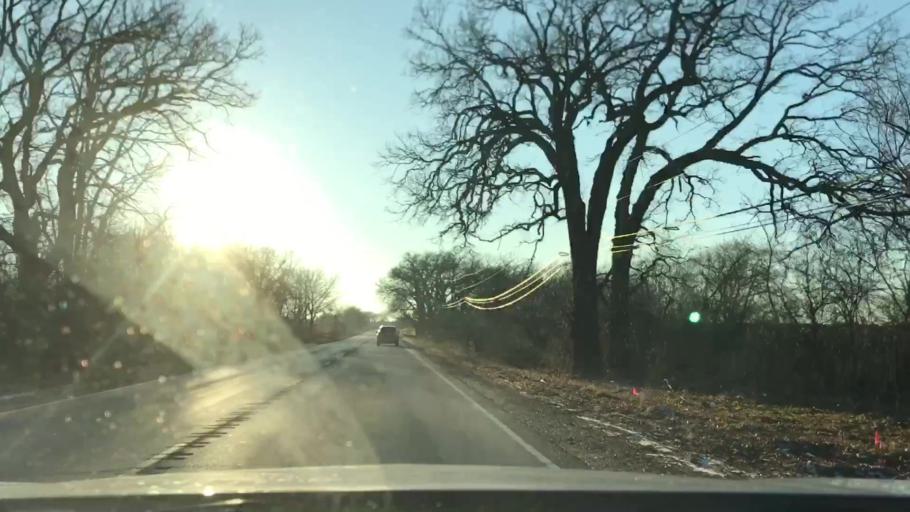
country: US
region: Illinois
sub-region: Kane County
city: Pingree Grove
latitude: 42.0932
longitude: -88.4165
